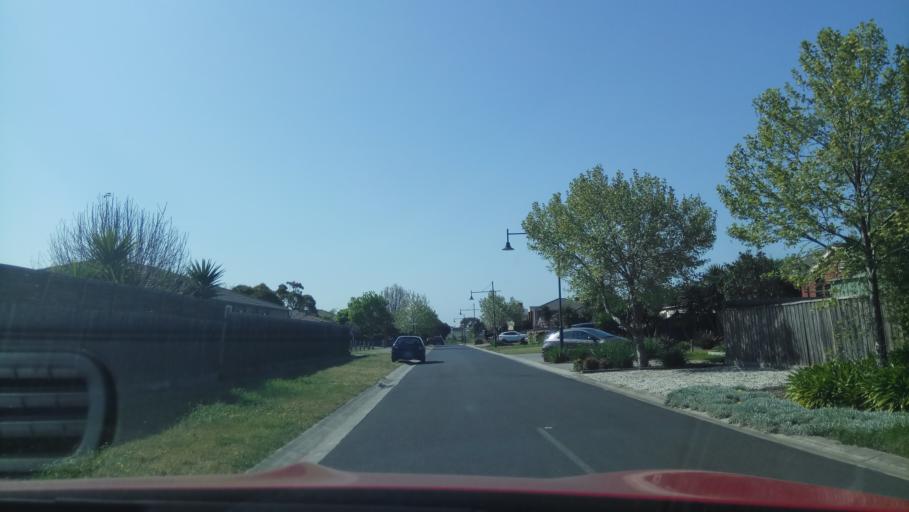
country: AU
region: Victoria
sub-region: Wyndham
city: Williams Landing
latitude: -37.8785
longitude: 144.7497
